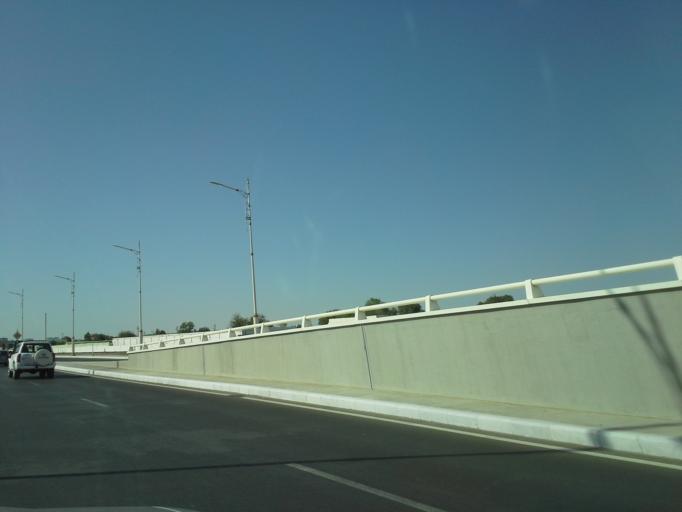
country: TM
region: Ahal
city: Ashgabat
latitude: 37.9304
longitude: 58.4199
